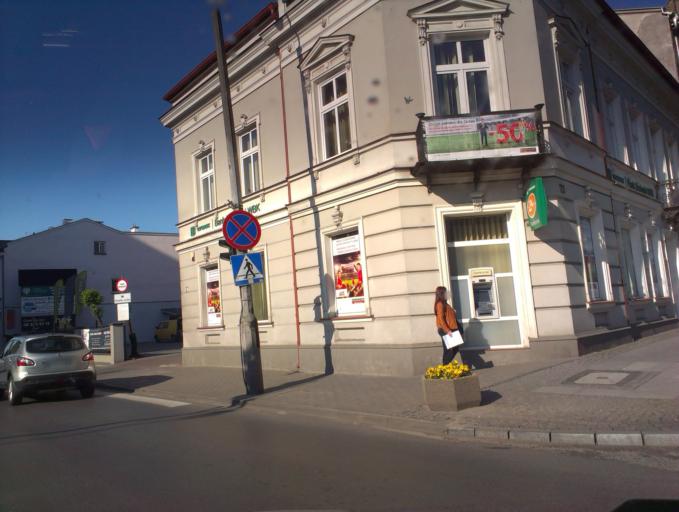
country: PL
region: Masovian Voivodeship
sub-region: Radom
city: Radom
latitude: 51.4001
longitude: 21.1626
